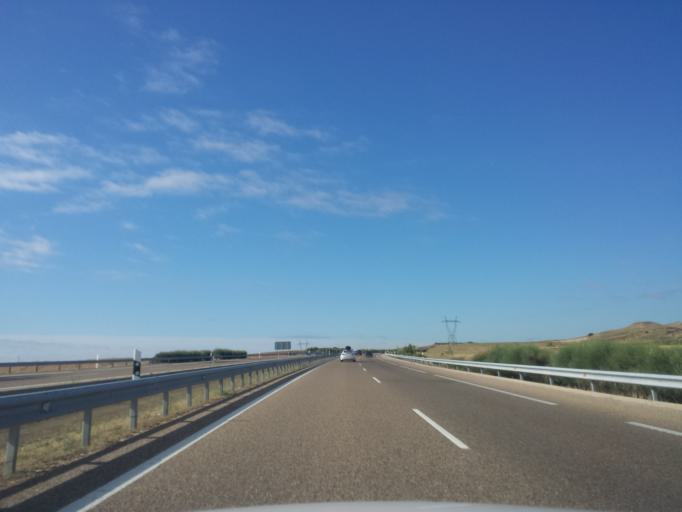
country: ES
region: Castille and Leon
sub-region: Provincia de Leon
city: Algadefe
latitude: 42.2347
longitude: -5.5926
